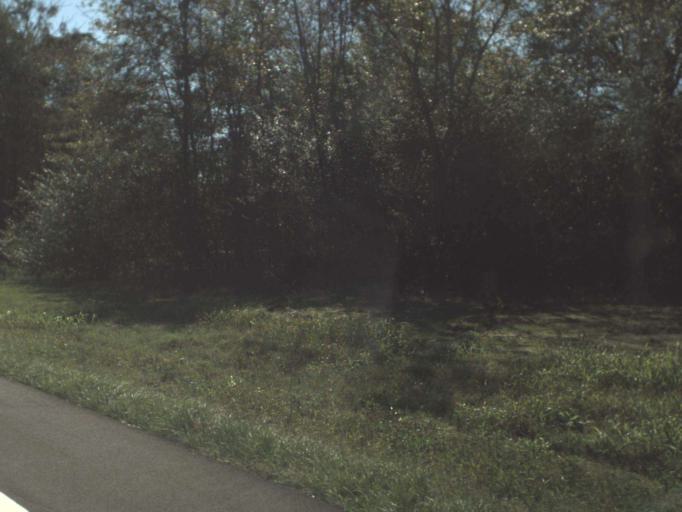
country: US
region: Alabama
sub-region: Escambia County
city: East Brewton
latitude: 30.9329
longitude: -87.0591
